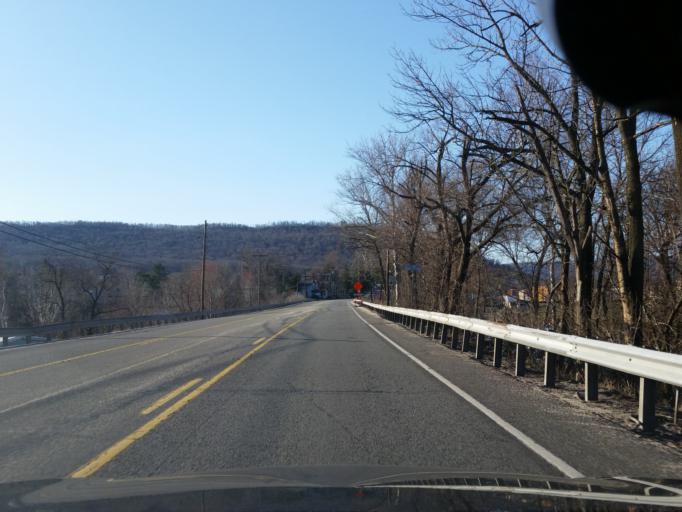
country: US
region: Pennsylvania
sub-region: Perry County
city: Marysville
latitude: 40.3374
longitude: -76.9273
